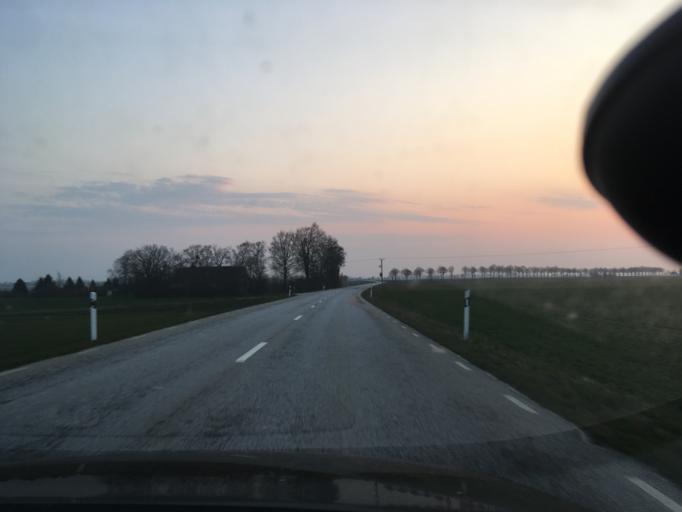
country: SE
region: Skane
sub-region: Ystads Kommun
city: Kopingebro
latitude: 55.4681
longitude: 14.0418
